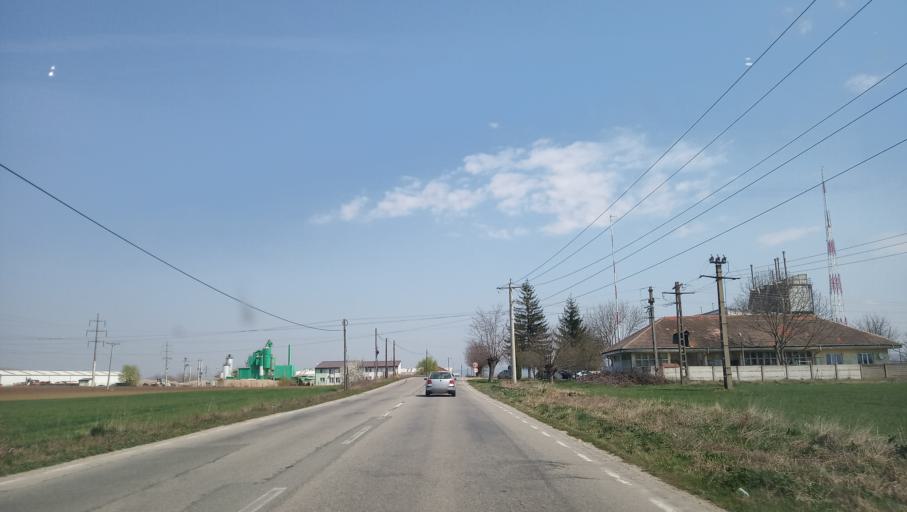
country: RO
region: Alba
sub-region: Municipiul Sebes
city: Lancram
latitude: 46.0180
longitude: 23.5192
